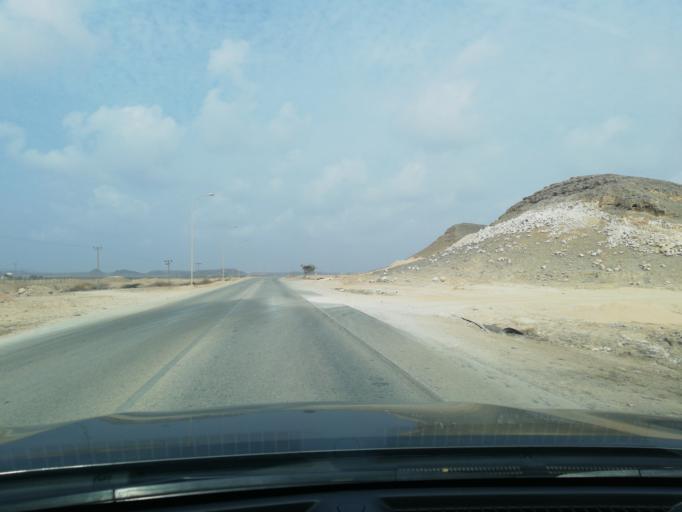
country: OM
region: Zufar
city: Salalah
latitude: 16.9461
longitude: 53.9521
